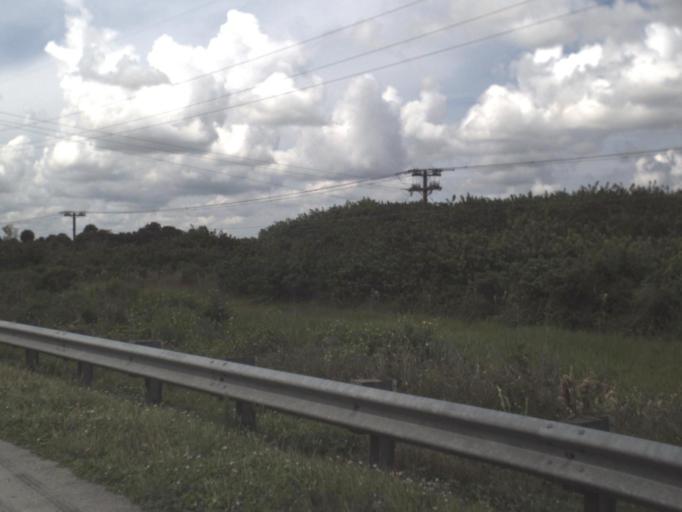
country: US
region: Florida
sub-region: Glades County
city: Buckhead Ridge
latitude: 27.2412
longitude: -80.9773
